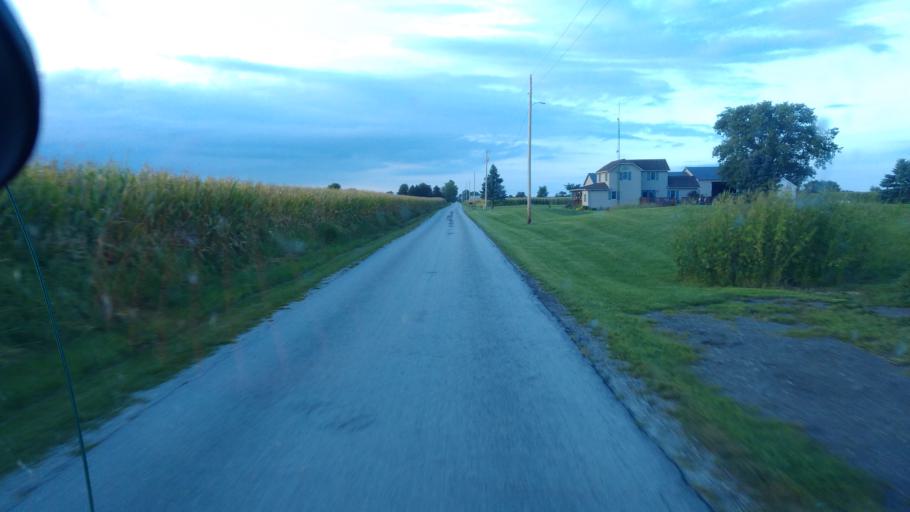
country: US
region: Ohio
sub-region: Hardin County
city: Kenton
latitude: 40.6285
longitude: -83.5157
